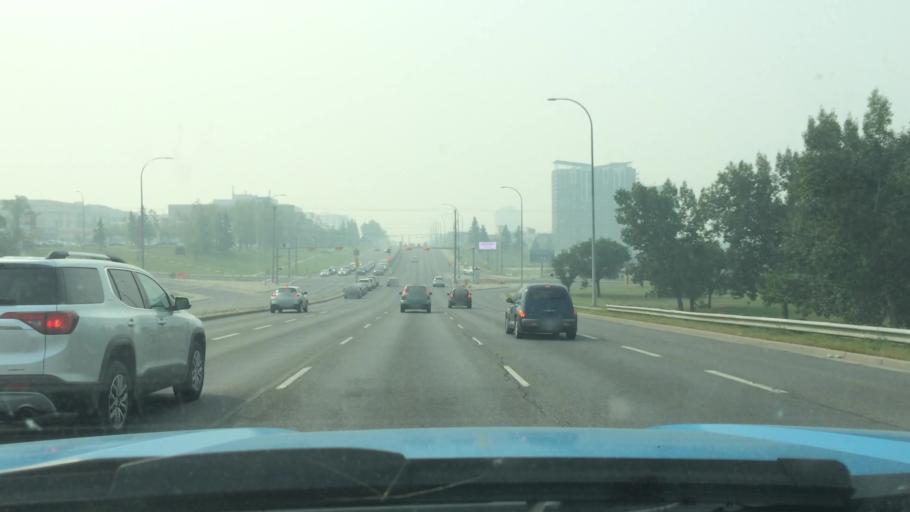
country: CA
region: Alberta
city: Calgary
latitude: 50.9811
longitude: -114.0720
